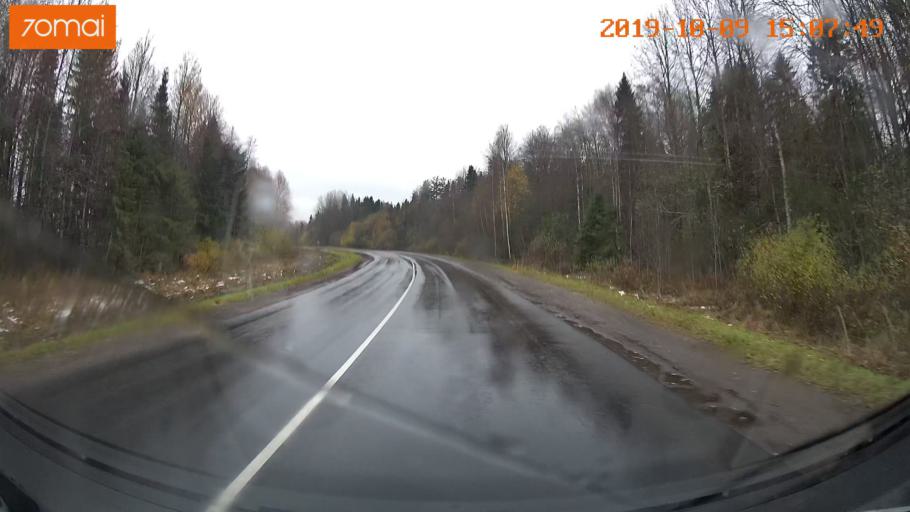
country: RU
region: Kostroma
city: Susanino
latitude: 58.2144
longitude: 41.6467
